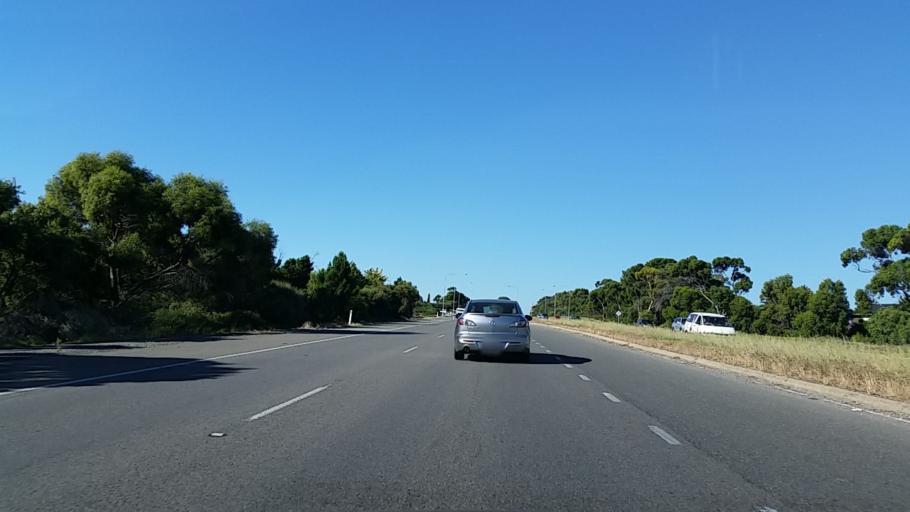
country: AU
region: South Australia
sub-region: Marion
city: Happy Valley
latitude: -35.0716
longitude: 138.5258
